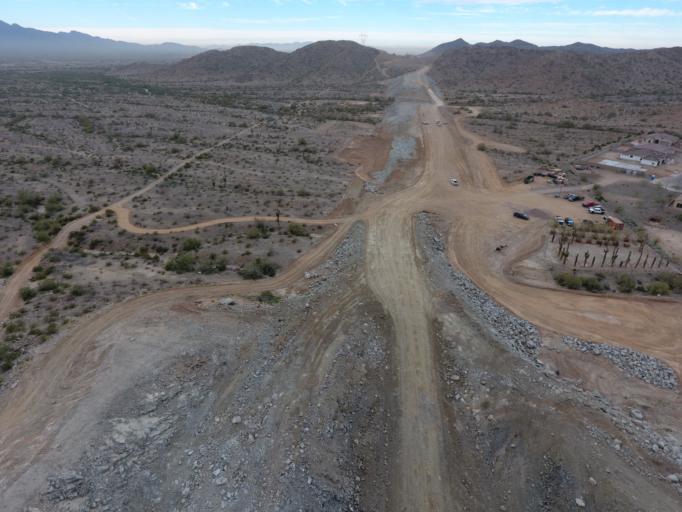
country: US
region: Arizona
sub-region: Maricopa County
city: Laveen
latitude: 33.2966
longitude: -112.1377
